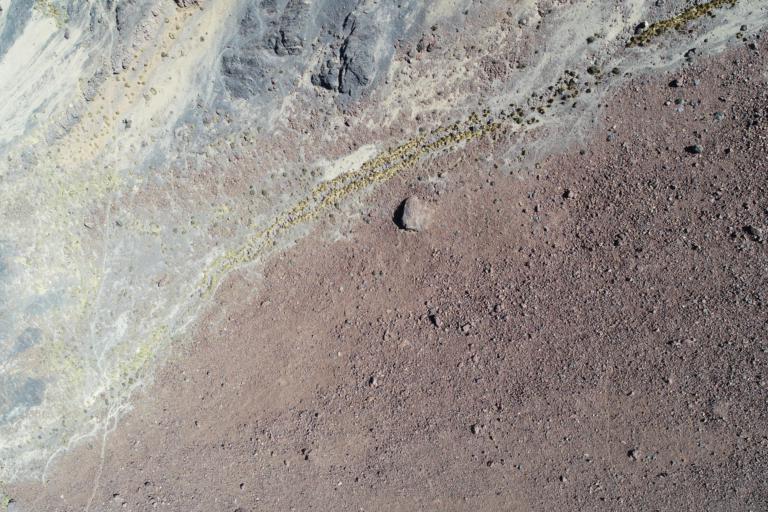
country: BO
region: La Paz
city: La Paz
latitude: -16.6200
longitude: -67.8226
